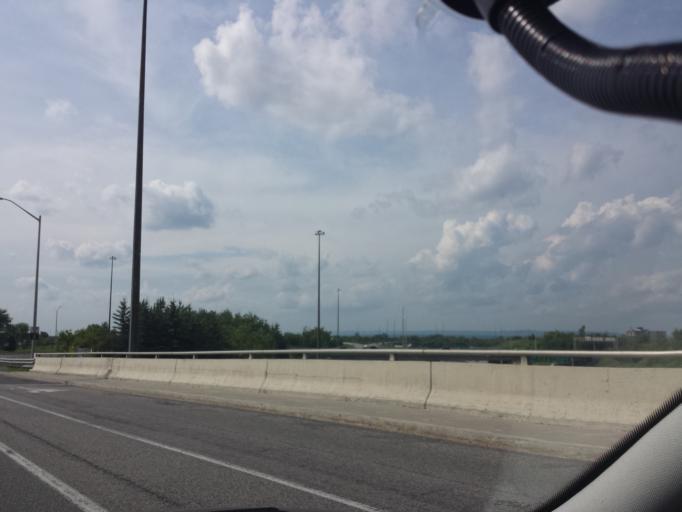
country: CA
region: Ontario
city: Bells Corners
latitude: 45.3337
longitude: -75.8112
